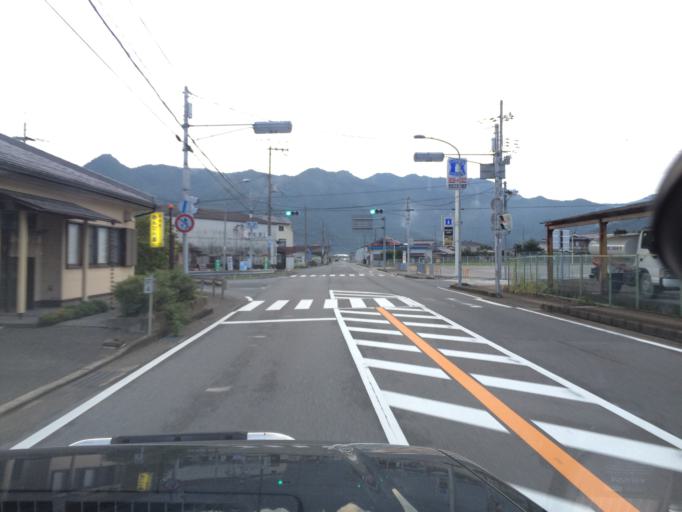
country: JP
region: Hyogo
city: Nishiwaki
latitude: 35.1007
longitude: 134.9963
